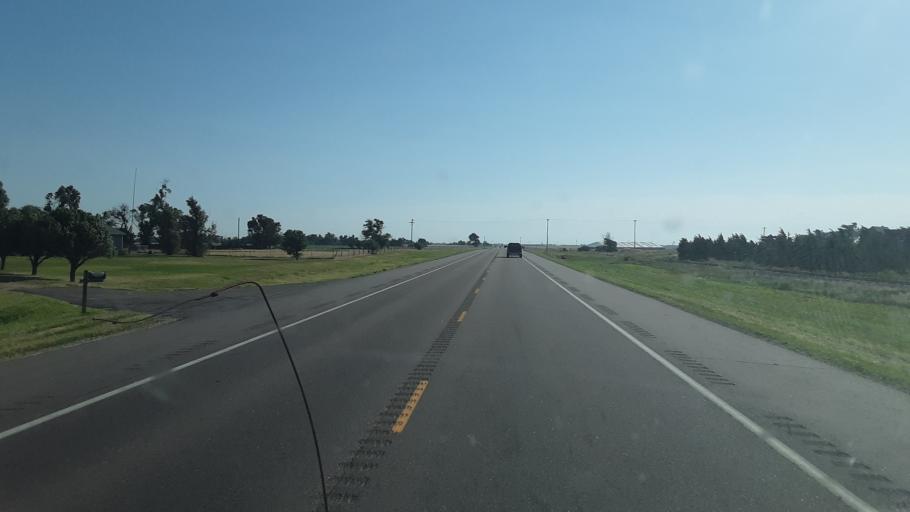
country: US
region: Kansas
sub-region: Pawnee County
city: Larned
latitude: 38.1987
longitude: -99.0717
